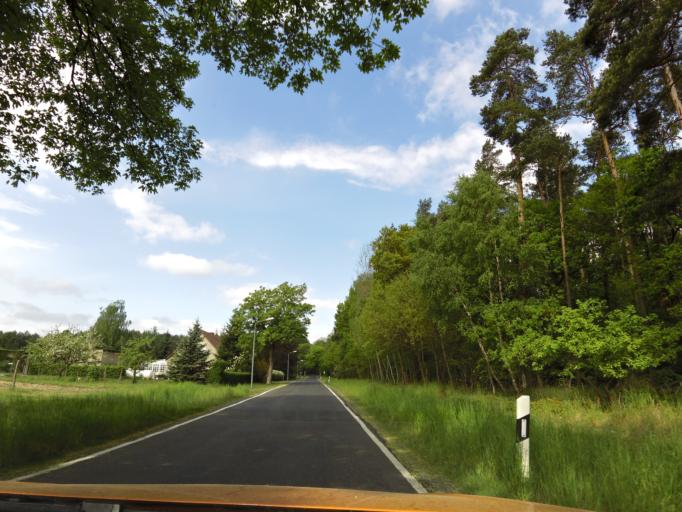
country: DE
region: Brandenburg
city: Wiesenburg
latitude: 52.0781
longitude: 12.5171
